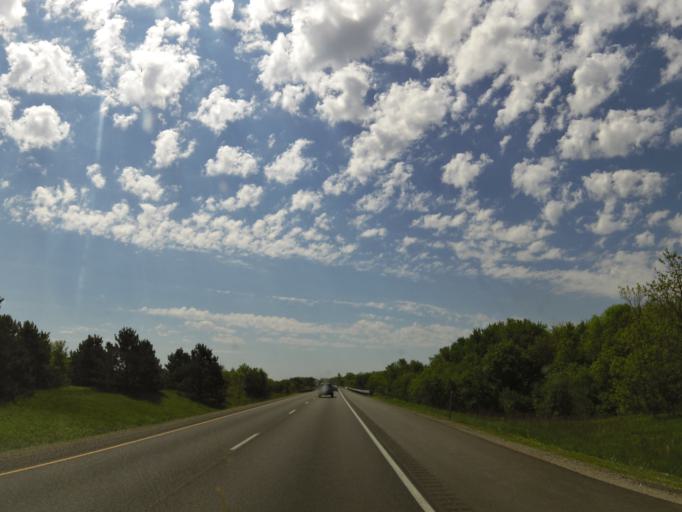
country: US
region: Wisconsin
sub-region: Eau Claire County
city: Fall Creek
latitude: 44.7036
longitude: -91.3433
